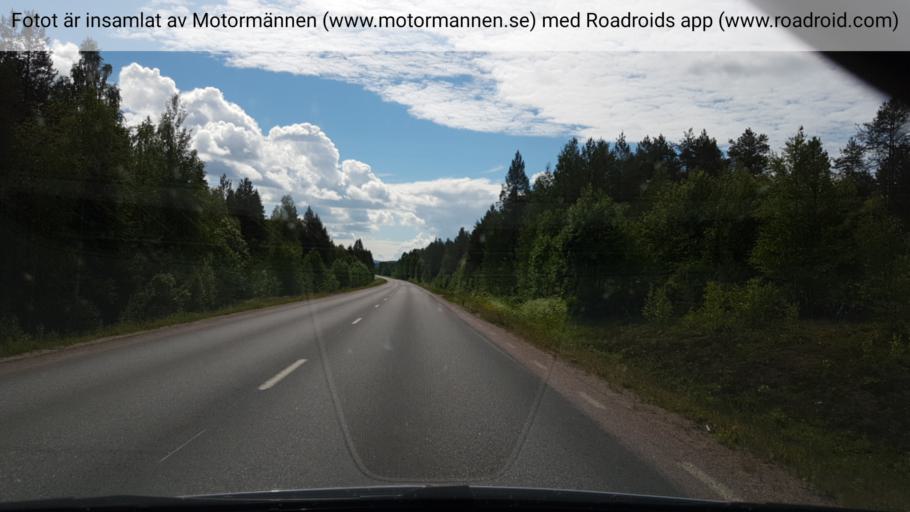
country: SE
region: Norrbotten
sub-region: Overtornea Kommun
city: OEvertornea
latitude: 66.4378
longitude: 23.6199
